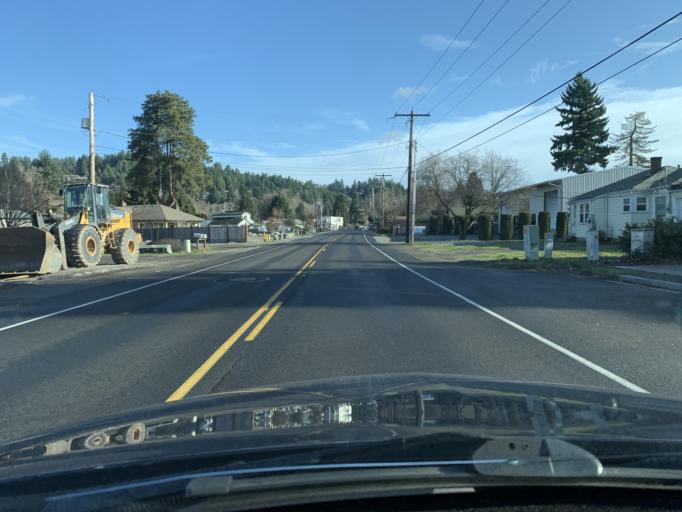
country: US
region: Washington
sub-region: Pierce County
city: North Puyallup
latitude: 47.2059
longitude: -122.2862
